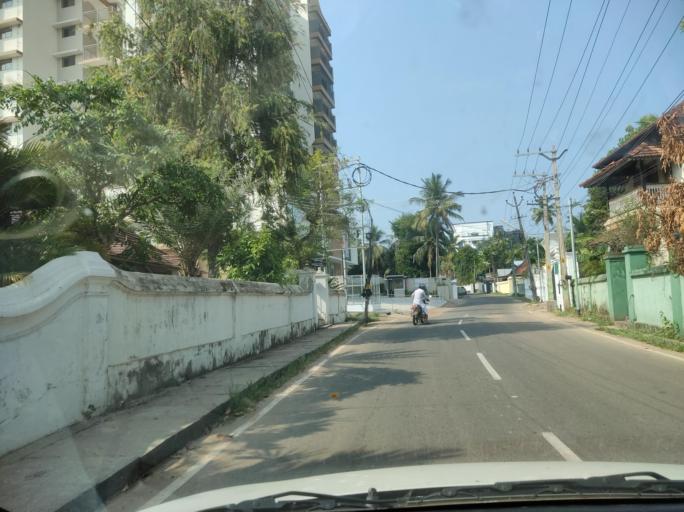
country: IN
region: Kerala
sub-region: Kottayam
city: Kottayam
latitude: 9.5911
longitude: 76.5114
